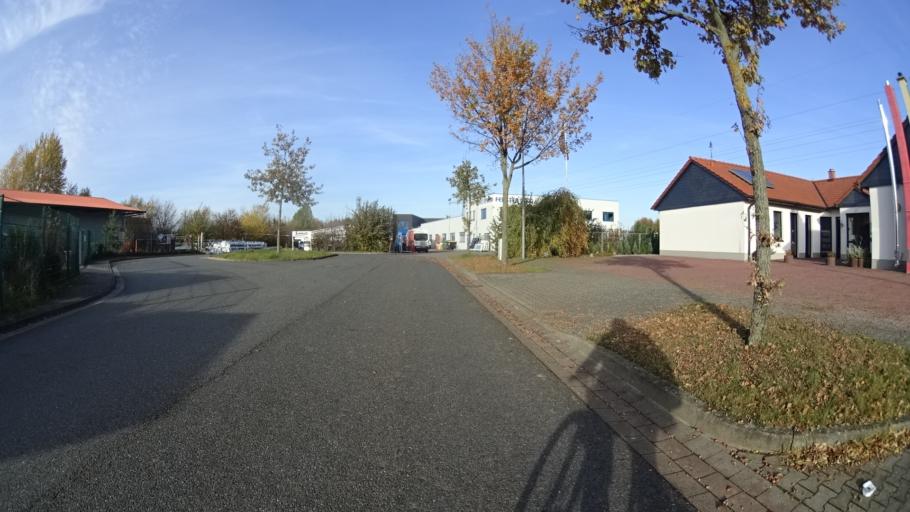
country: DE
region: Lower Saxony
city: Wendisch Evern
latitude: 53.2386
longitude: 10.4649
